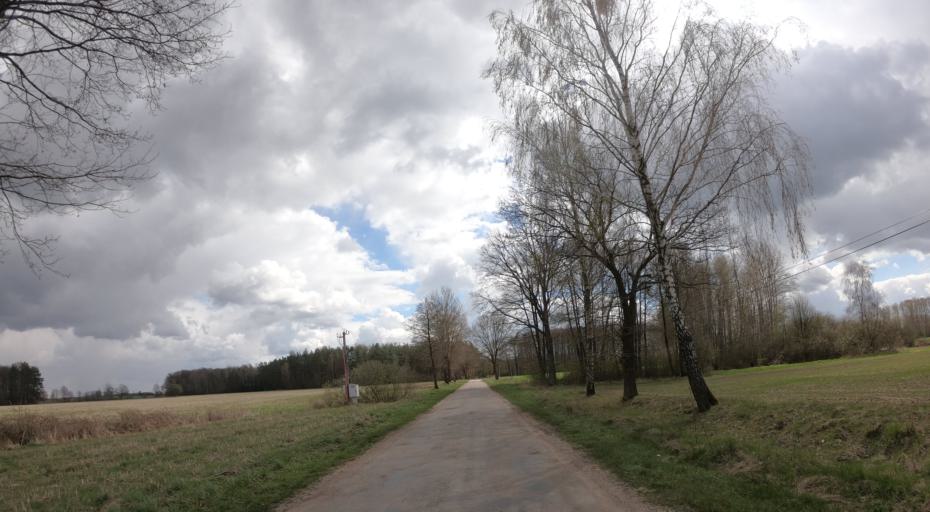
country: PL
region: West Pomeranian Voivodeship
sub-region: Powiat drawski
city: Drawsko Pomorskie
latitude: 53.5369
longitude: 15.8848
